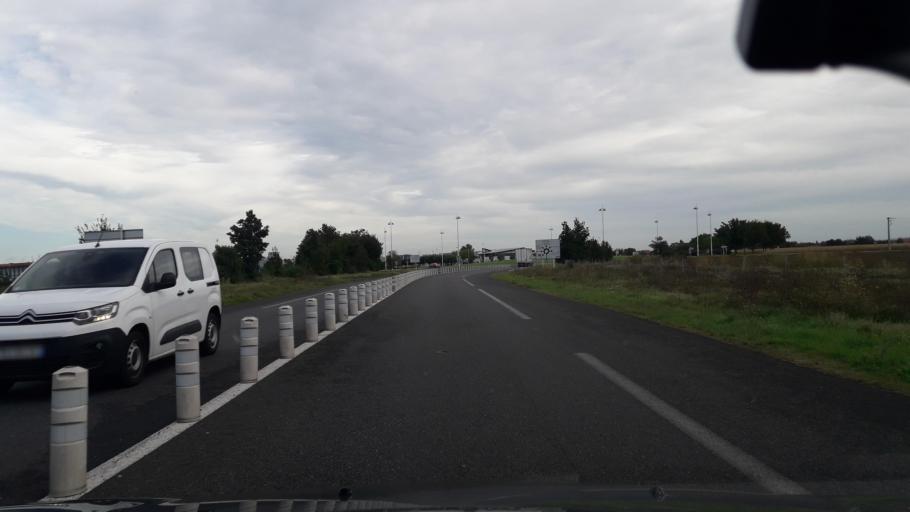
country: FR
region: Auvergne
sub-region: Departement du Puy-de-Dome
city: Gerzat
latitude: 45.8444
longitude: 3.1647
